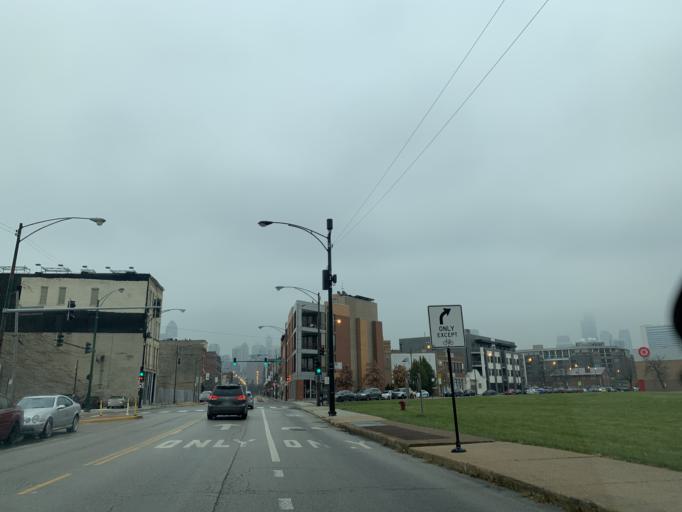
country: US
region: Illinois
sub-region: Cook County
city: Chicago
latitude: 41.9069
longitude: -87.6439
